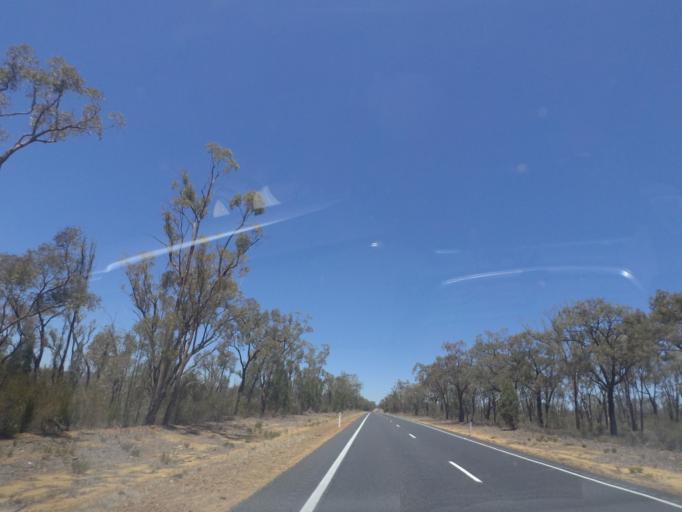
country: AU
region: New South Wales
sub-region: Narrabri
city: Narrabri
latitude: -30.7449
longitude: 149.5135
